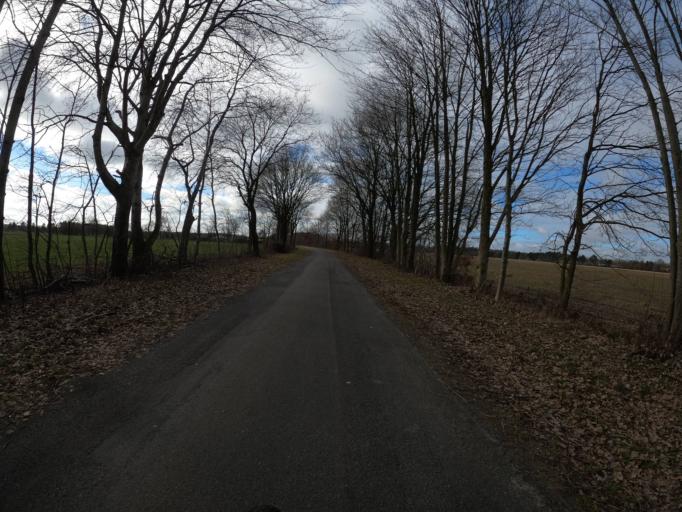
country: DE
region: Lower Saxony
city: Herzlake
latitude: 52.6835
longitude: 7.5839
